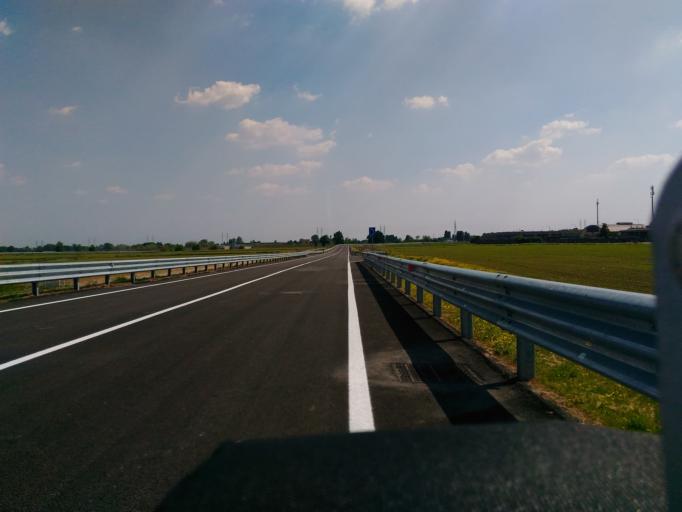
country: IT
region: Lombardy
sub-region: Citta metropolitana di Milano
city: Dresano
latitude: 45.3734
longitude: 9.3652
